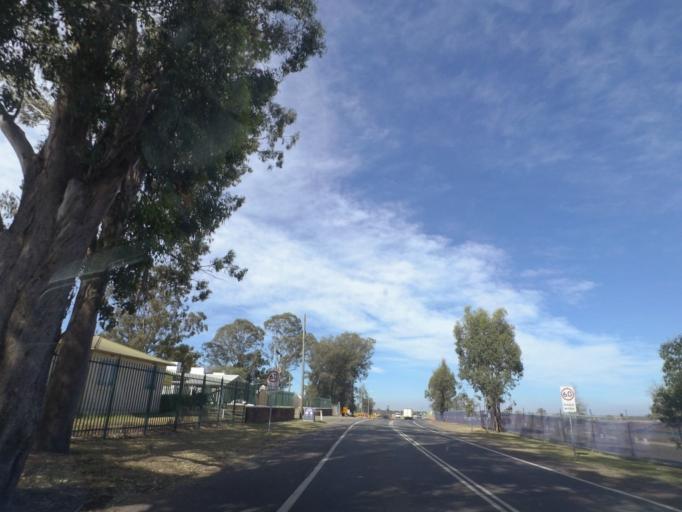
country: AU
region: New South Wales
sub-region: Campbelltown Municipality
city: Denham Court
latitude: -33.9758
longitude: 150.8530
